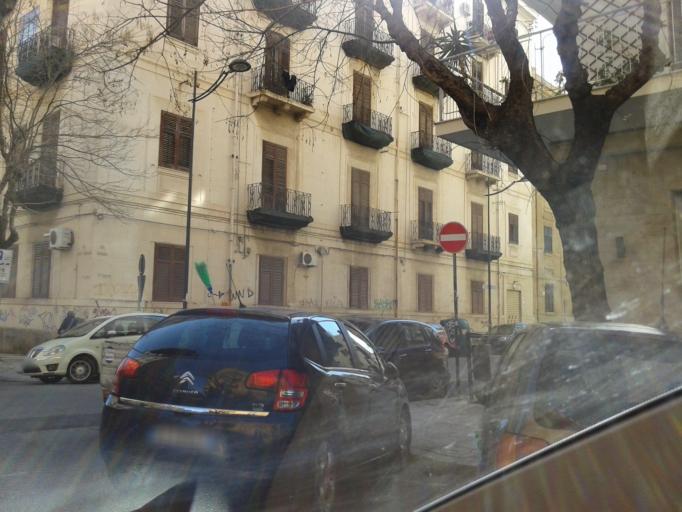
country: IT
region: Sicily
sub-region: Palermo
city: Palermo
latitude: 38.1355
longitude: 13.3472
